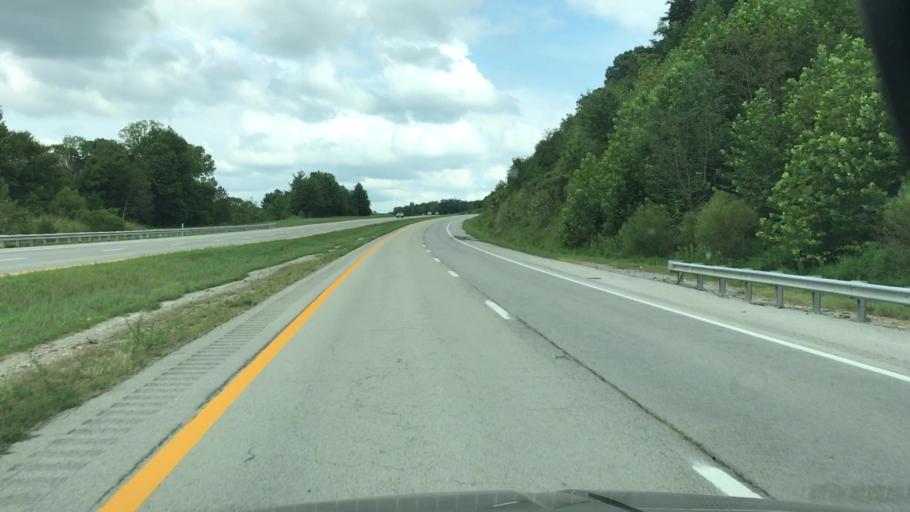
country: US
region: Kentucky
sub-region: Caldwell County
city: Princeton
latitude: 37.1407
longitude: -87.8223
